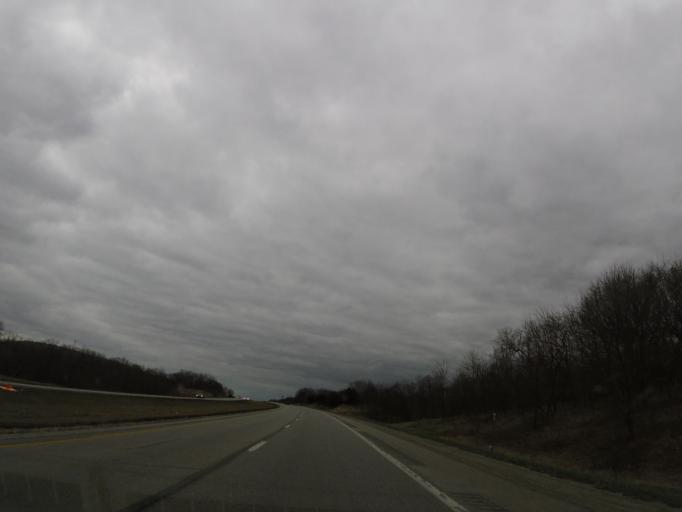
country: US
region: Iowa
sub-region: Johnson County
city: Tiffin
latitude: 41.6799
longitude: -91.6299
